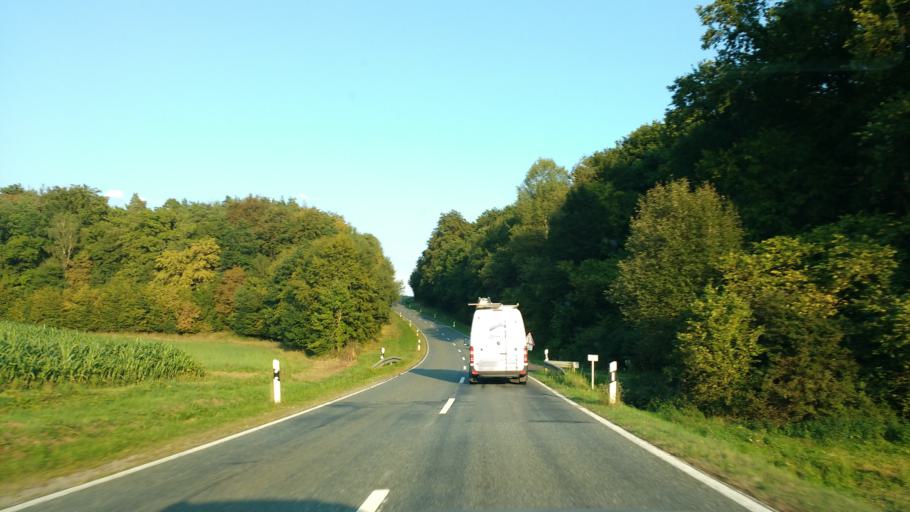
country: DE
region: Bavaria
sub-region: Regierungsbezirk Unterfranken
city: Wasserlosen
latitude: 50.0823
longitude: 9.9979
